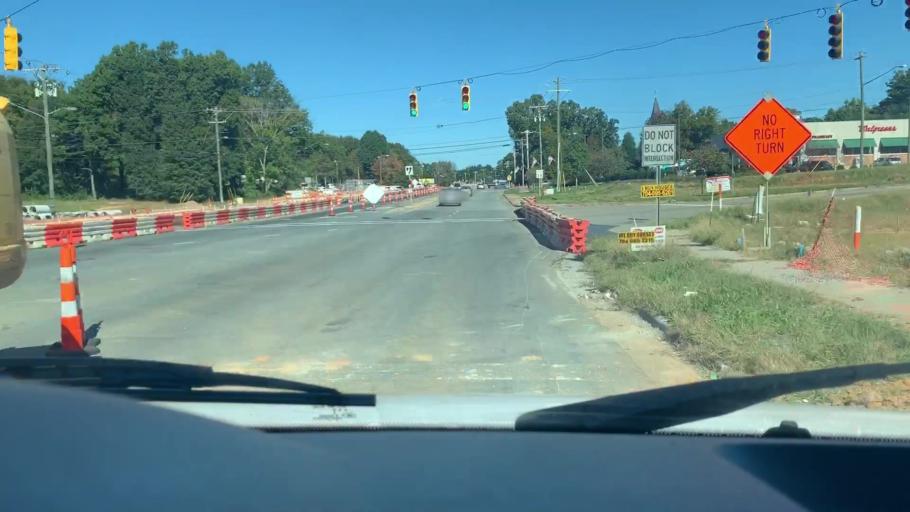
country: US
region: North Carolina
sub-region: Mecklenburg County
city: Charlotte
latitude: 35.2920
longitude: -80.7964
